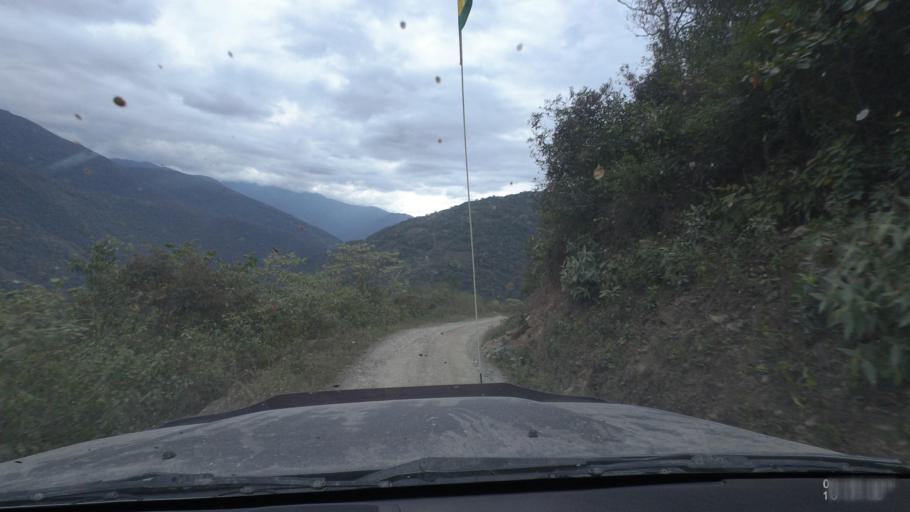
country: BO
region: La Paz
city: Quime
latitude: -16.5382
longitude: -66.7610
